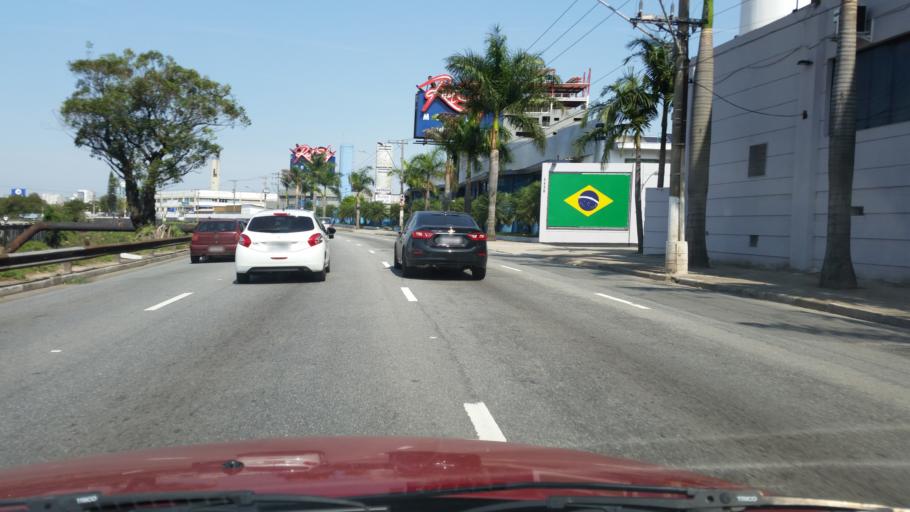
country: BR
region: Sao Paulo
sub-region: Santo Andre
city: Santo Andre
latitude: -23.6434
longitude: -46.5326
